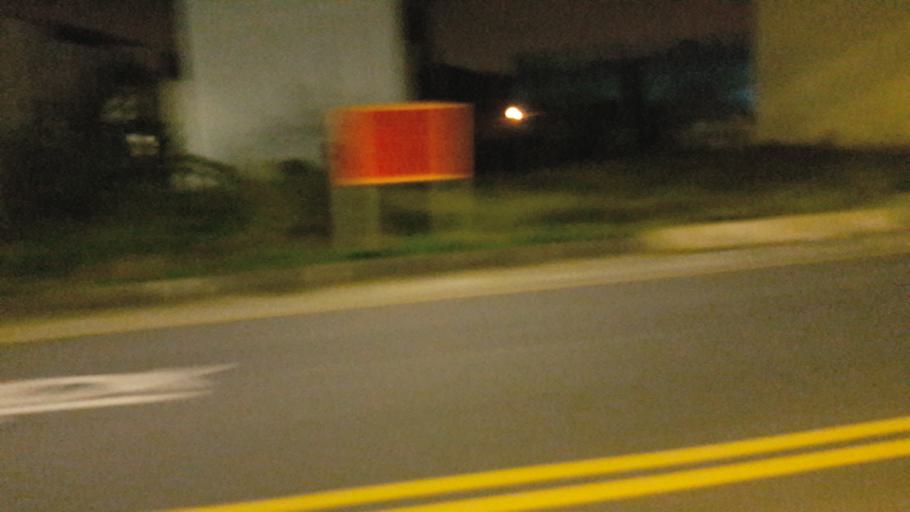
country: TW
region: Taiwan
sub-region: Hsinchu
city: Hsinchu
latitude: 24.7676
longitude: 120.9792
